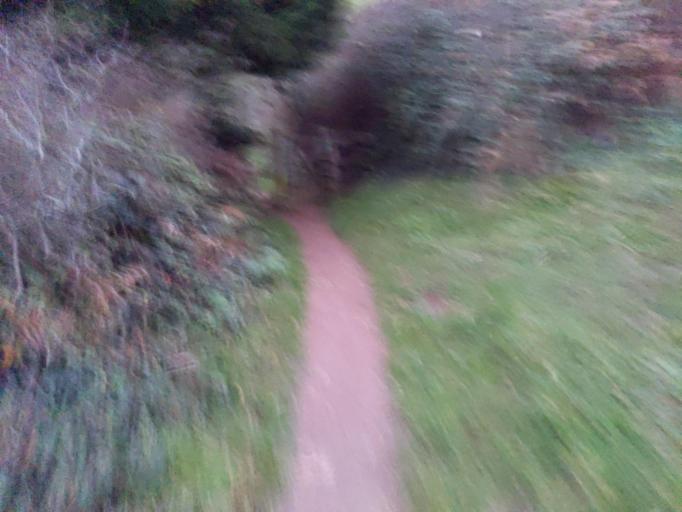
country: GB
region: England
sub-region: Cornwall
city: Millbrook
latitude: 50.3217
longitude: -4.2189
